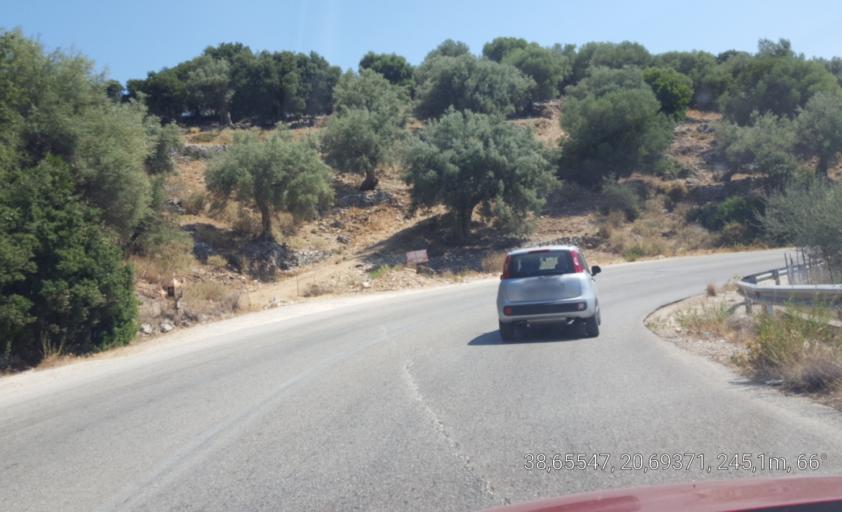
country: GR
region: Ionian Islands
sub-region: Lefkada
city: Nidri
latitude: 38.6555
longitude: 20.6937
